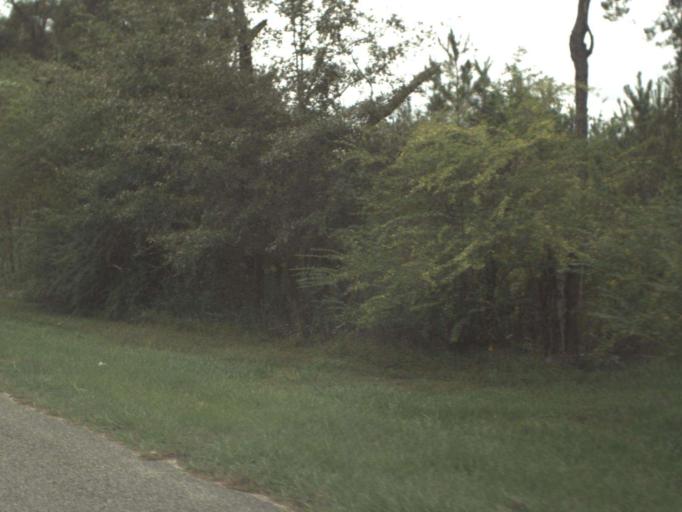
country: US
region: Florida
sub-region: Jackson County
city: Marianna
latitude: 30.6062
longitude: -85.1812
